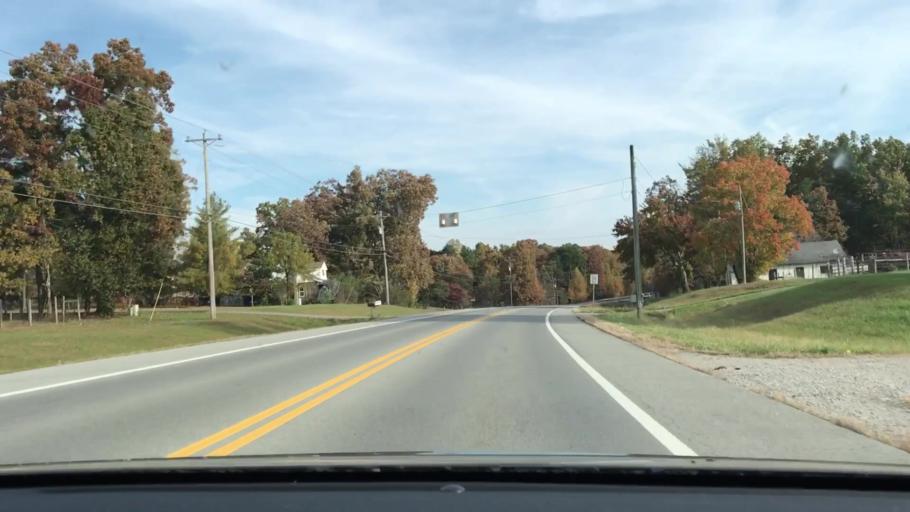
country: US
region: Tennessee
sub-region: Fentress County
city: Grimsley
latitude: 36.2404
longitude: -85.0058
